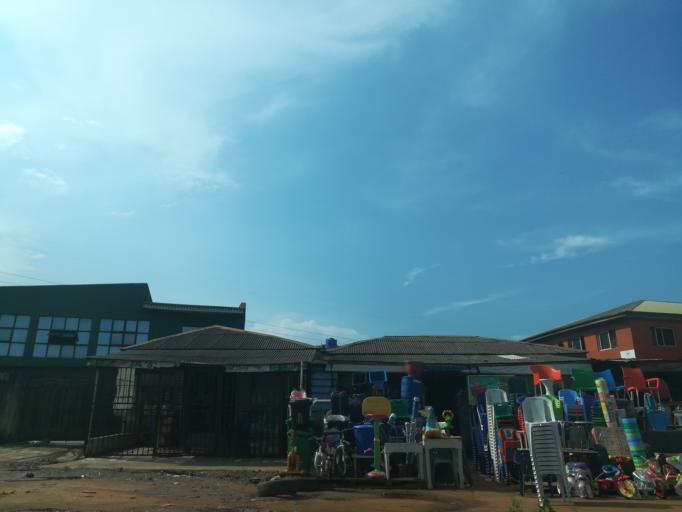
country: NG
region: Lagos
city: Ikorodu
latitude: 6.6289
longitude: 3.5107
